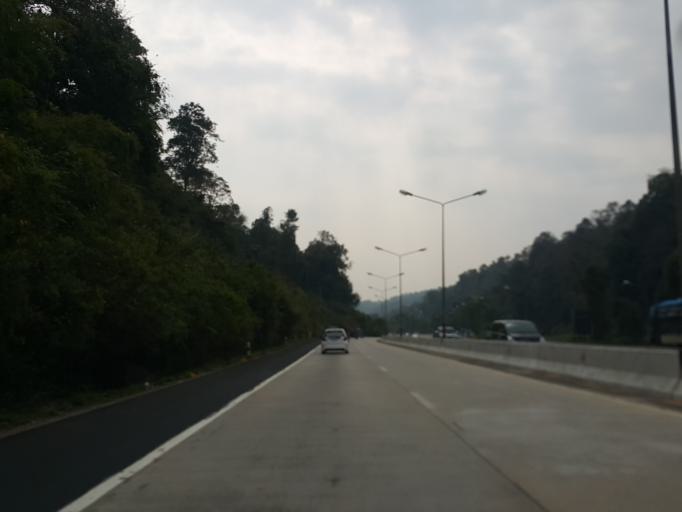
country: TH
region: Lamphun
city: Mae Tha
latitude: 18.3912
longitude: 99.2173
